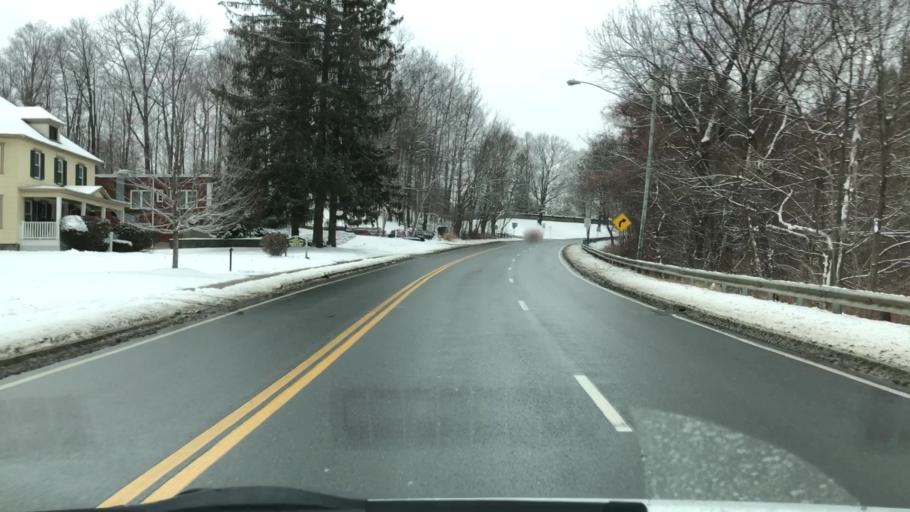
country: US
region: Massachusetts
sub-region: Berkshire County
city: Dalton
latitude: 42.4721
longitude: -73.1775
